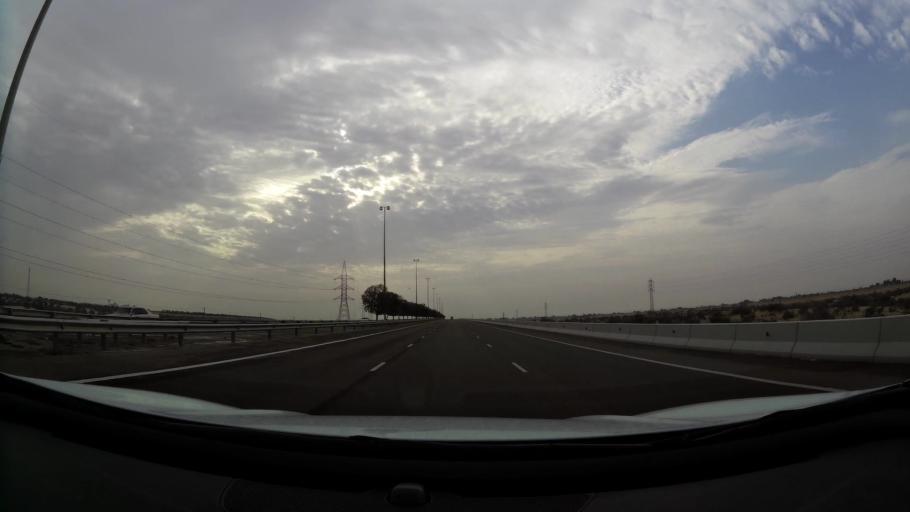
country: AE
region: Abu Dhabi
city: Abu Dhabi
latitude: 24.2087
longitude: 54.8938
